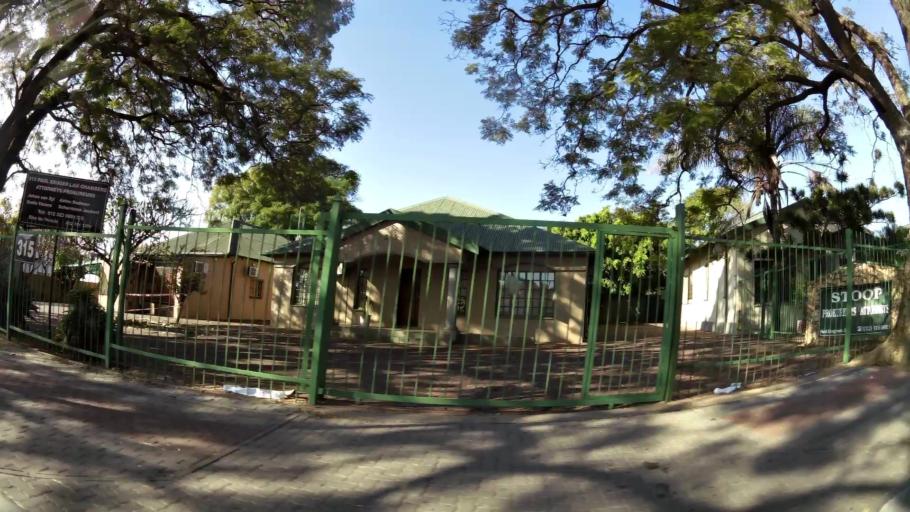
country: ZA
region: Gauteng
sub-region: City of Tshwane Metropolitan Municipality
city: Pretoria
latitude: -25.7266
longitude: 28.1886
